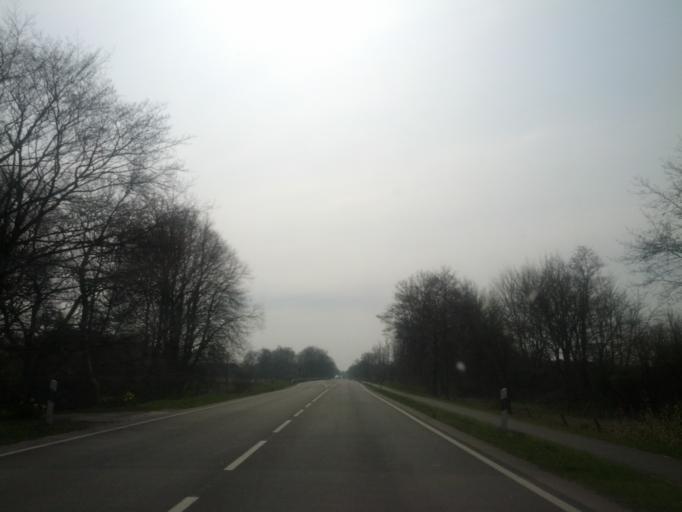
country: DE
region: Lower Saxony
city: Osteel
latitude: 53.5416
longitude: 7.2599
